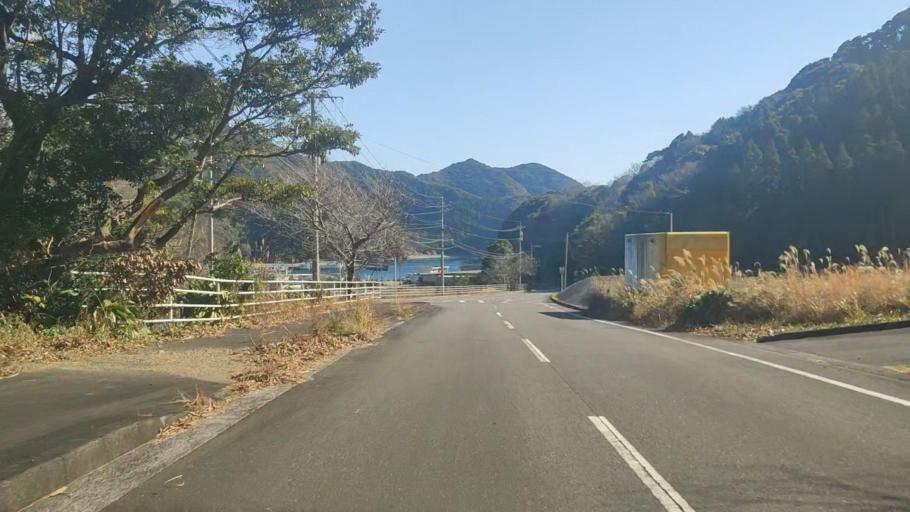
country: JP
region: Oita
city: Saiki
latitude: 32.7942
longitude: 131.9024
